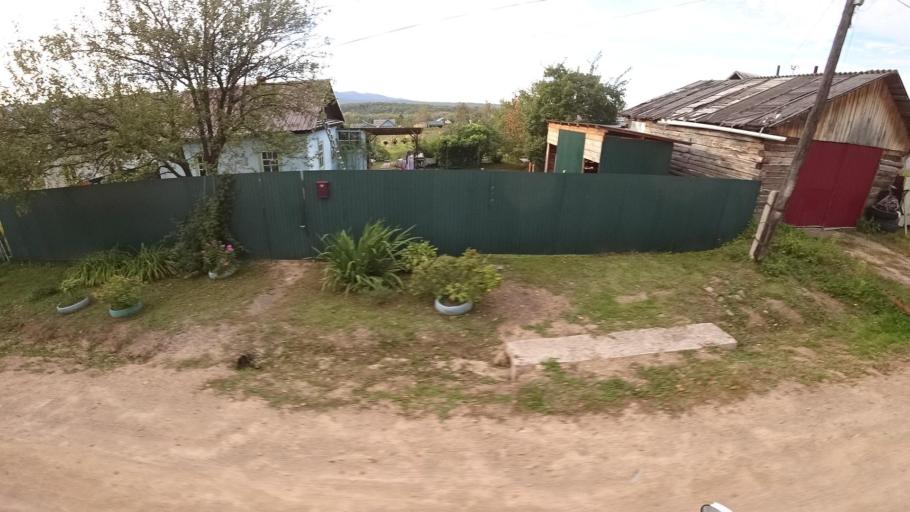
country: RU
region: Primorskiy
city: Yakovlevka
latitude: 44.4129
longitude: 133.4516
